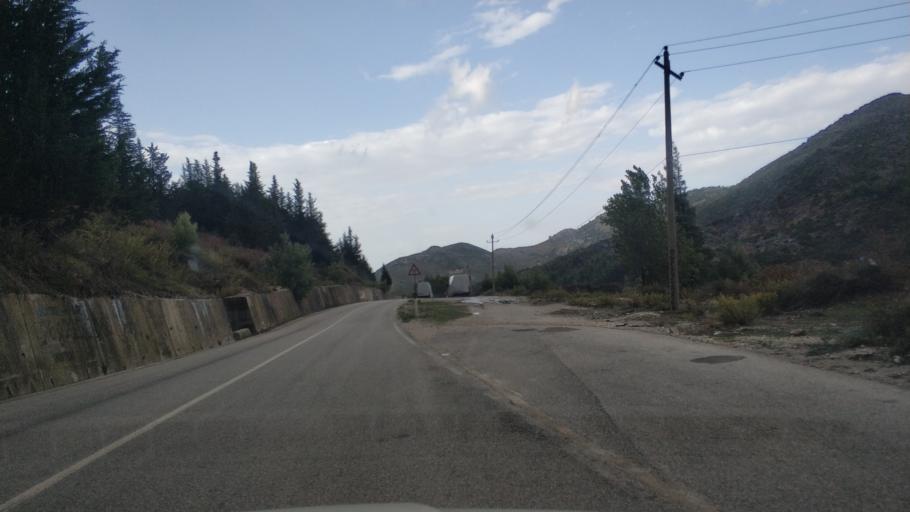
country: AL
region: Vlore
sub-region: Rrethi i Vlores
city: Orikum
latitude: 40.2599
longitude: 19.5245
